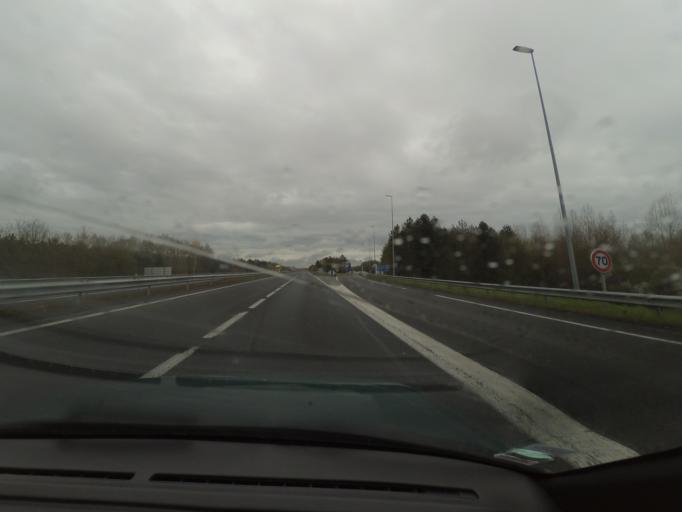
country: FR
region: Pays de la Loire
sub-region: Departement de la Sarthe
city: Parce-sur-Sarthe
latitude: 47.8015
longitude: -0.1705
